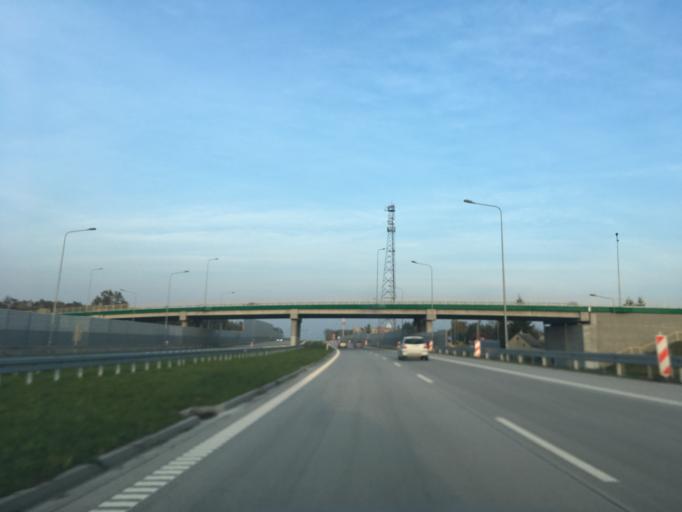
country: PL
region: Lodz Voivodeship
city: Zabia Wola
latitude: 52.0268
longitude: 20.6677
